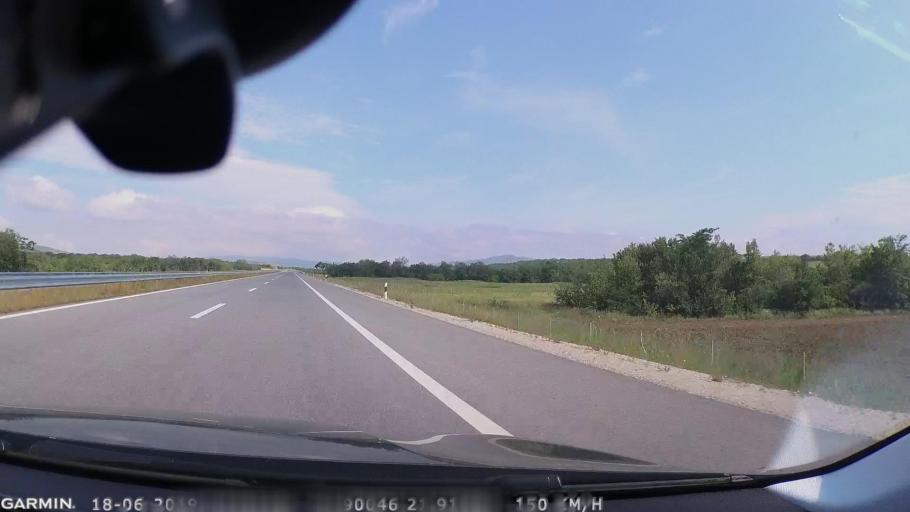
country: MK
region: Sveti Nikole
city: Gorobinci
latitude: 41.9021
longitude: 21.9138
